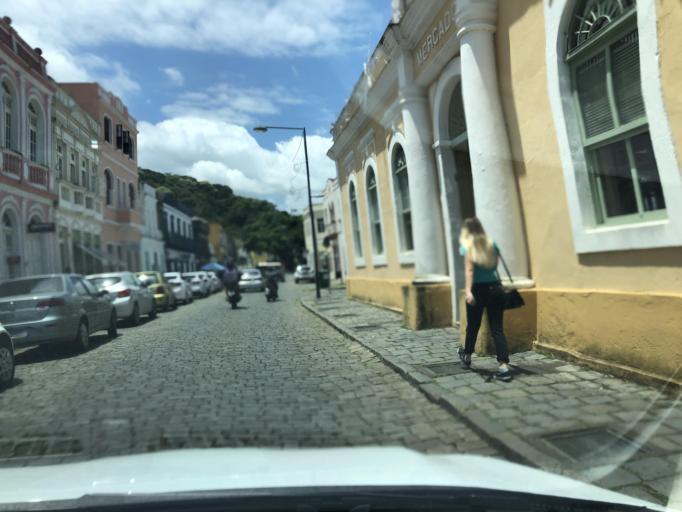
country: BR
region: Santa Catarina
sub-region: Sao Francisco Do Sul
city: Sao Francisco do Sul
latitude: -26.2431
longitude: -48.6397
